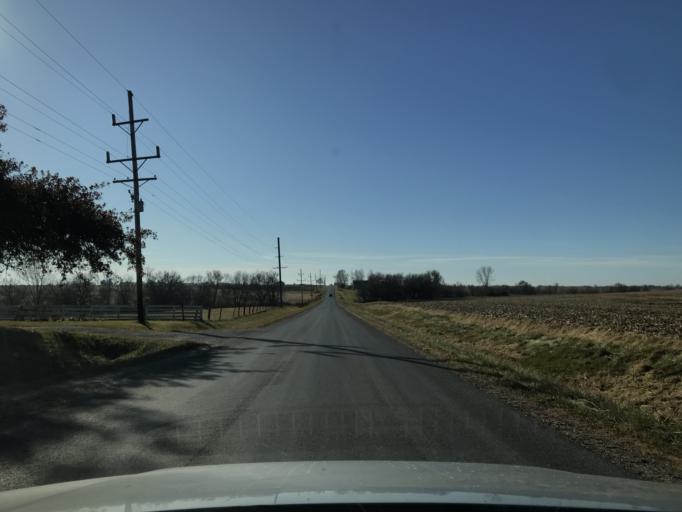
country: US
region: Illinois
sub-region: Hancock County
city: Carthage
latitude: 40.4907
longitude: -91.1779
